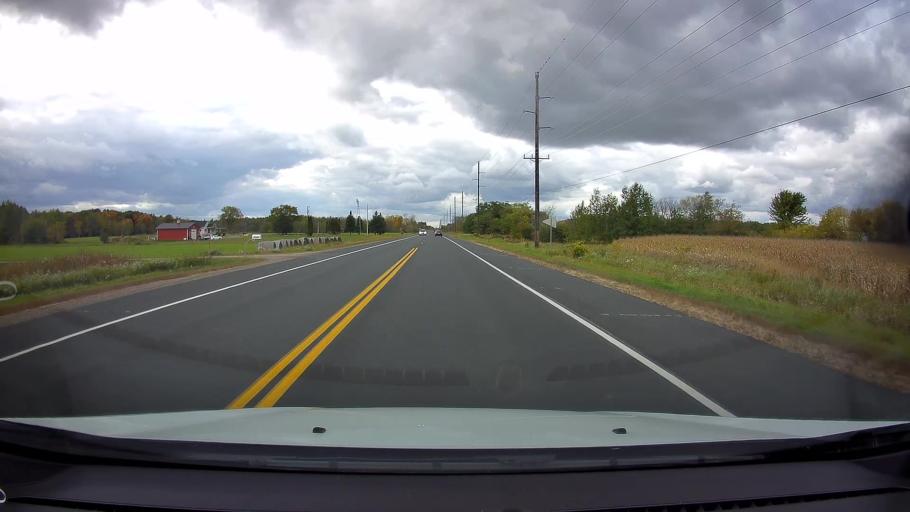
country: US
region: Minnesota
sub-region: Chisago County
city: Shafer
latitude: 45.3973
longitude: -92.7526
